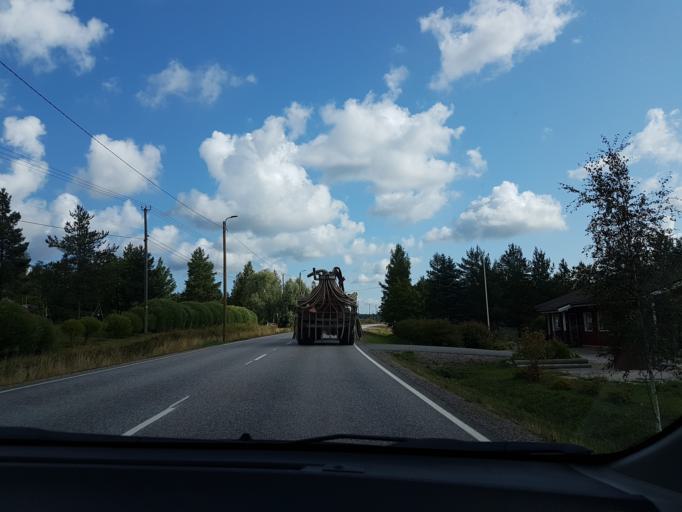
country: FI
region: Uusimaa
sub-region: Helsinki
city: Pornainen
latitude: 60.4825
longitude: 25.3417
